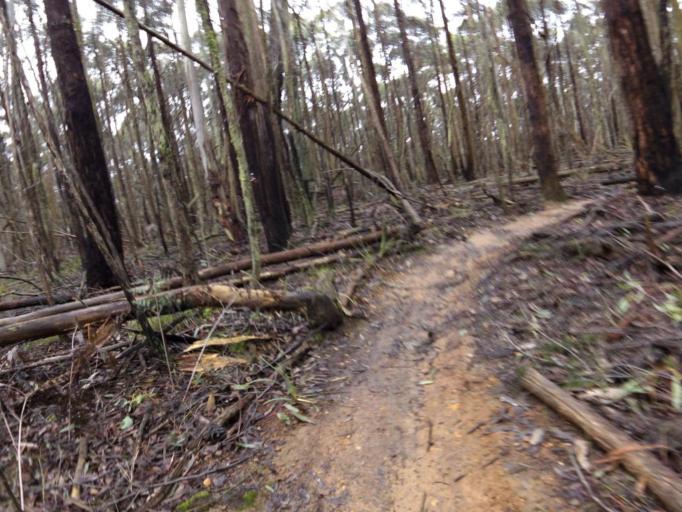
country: AU
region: Victoria
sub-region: Moorabool
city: Bacchus Marsh
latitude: -37.4198
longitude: 144.4893
